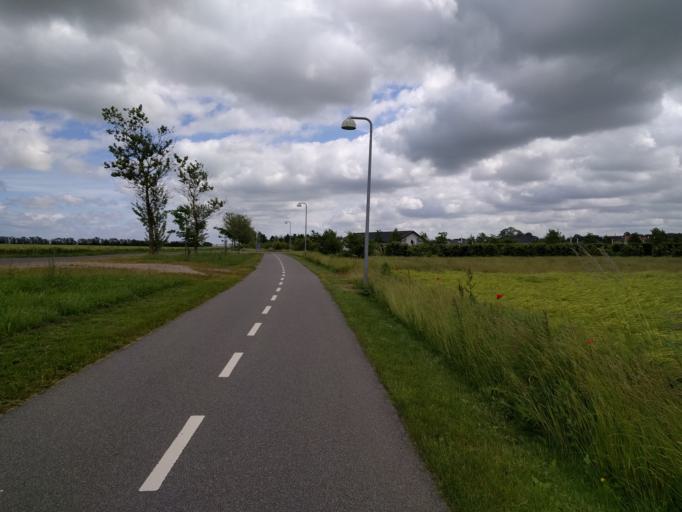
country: DK
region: South Denmark
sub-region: Odense Kommune
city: Bullerup
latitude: 55.4099
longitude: 10.4592
